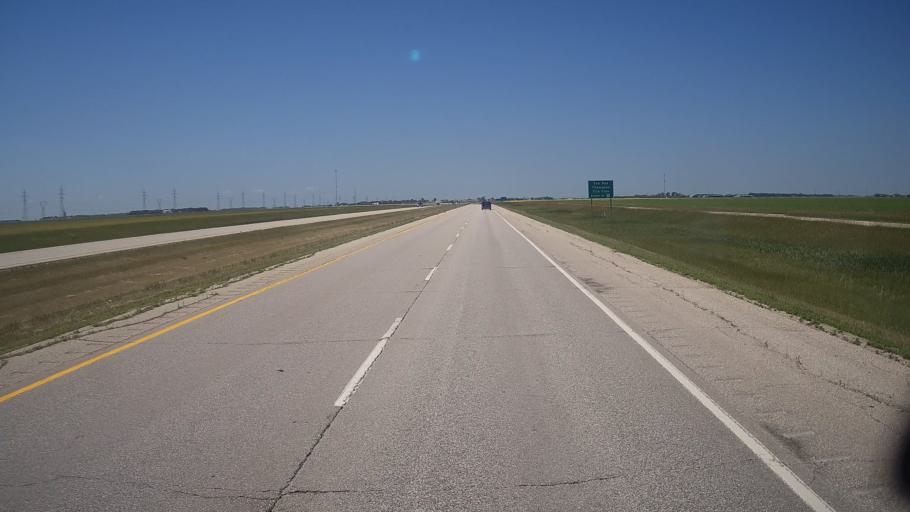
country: CA
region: Manitoba
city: Stonewall
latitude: 49.9900
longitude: -97.2868
